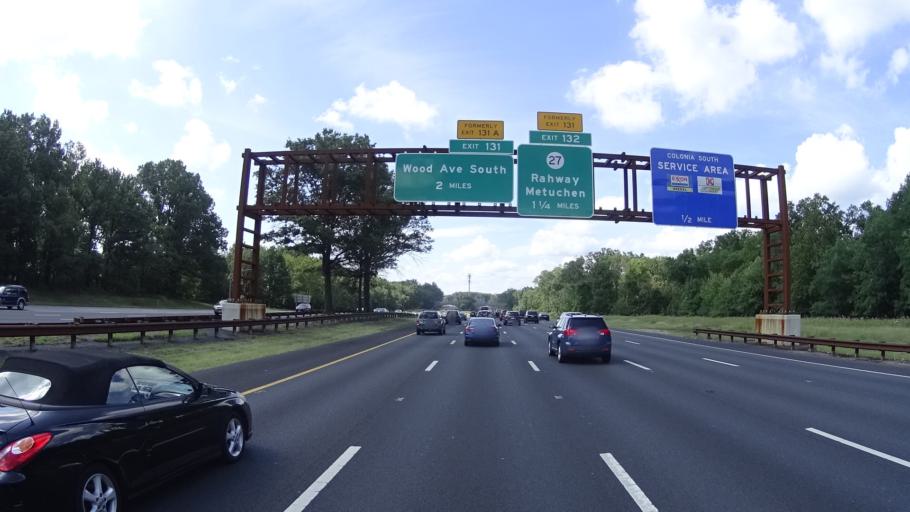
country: US
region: New Jersey
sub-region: Middlesex County
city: Iselin
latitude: 40.5901
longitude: -74.3254
